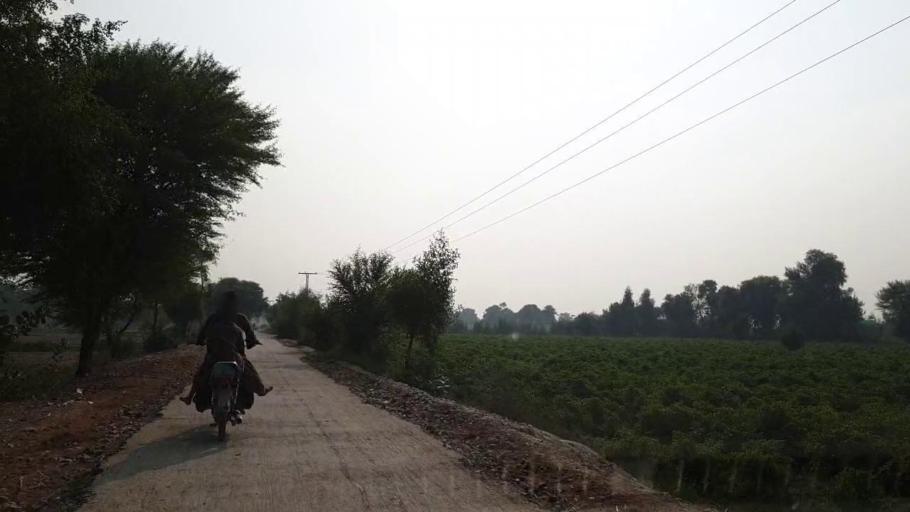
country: PK
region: Sindh
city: Bhan
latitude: 26.5830
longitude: 67.7304
